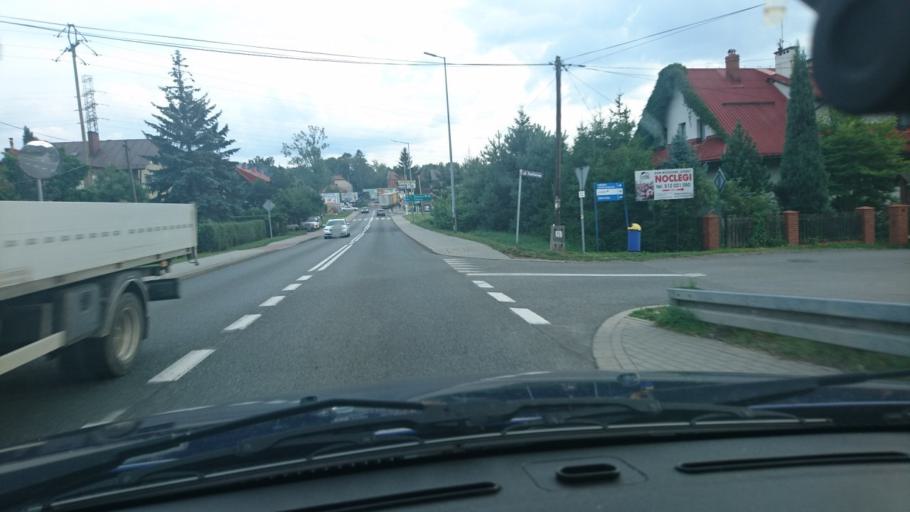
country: PL
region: Silesian Voivodeship
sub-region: Powiat zywiecki
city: Wegierska Gorka
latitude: 49.6081
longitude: 19.1163
